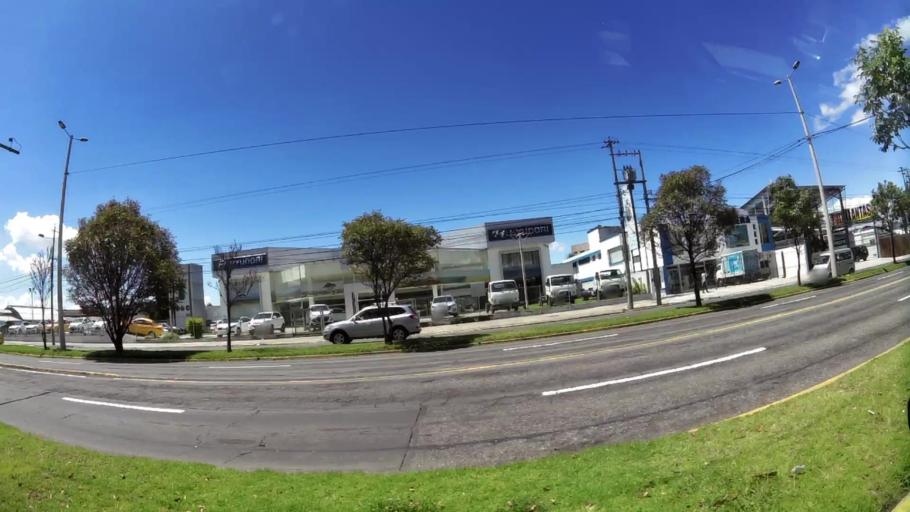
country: EC
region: Pichincha
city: Quito
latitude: -0.1591
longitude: -78.4855
